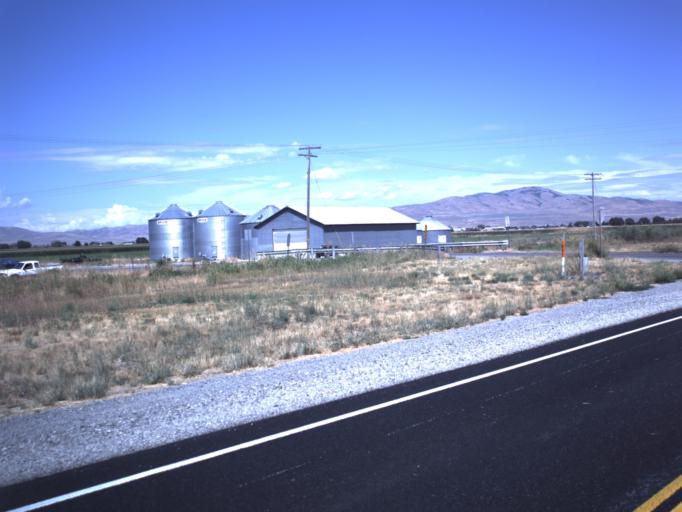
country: US
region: Utah
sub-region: Box Elder County
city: Elwood
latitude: 41.6537
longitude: -112.1402
